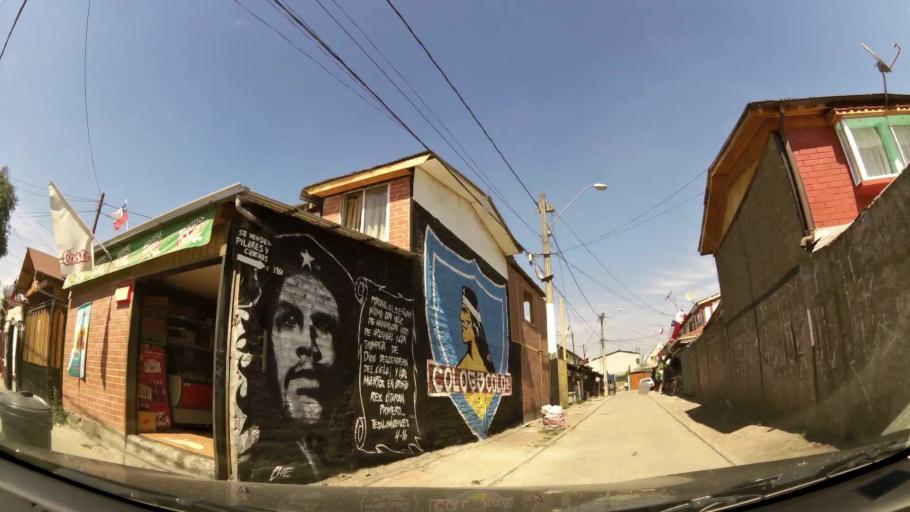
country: CL
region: Santiago Metropolitan
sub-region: Provincia de Santiago
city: La Pintana
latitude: -33.5932
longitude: -70.6213
